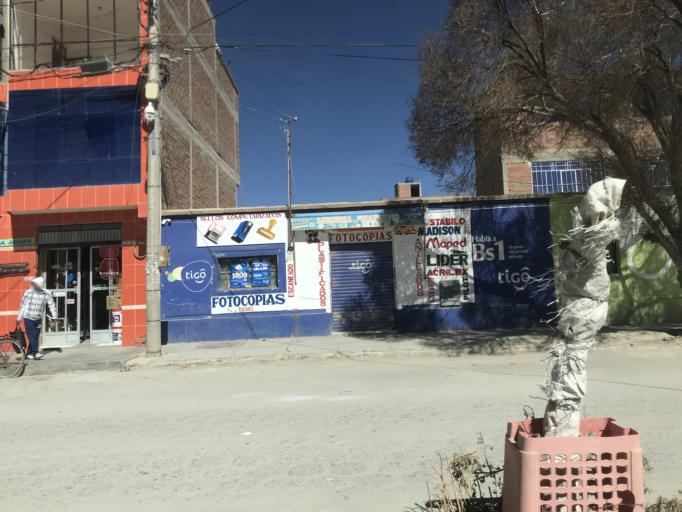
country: BO
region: Potosi
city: Uyuni
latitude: -20.4584
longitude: -66.8258
